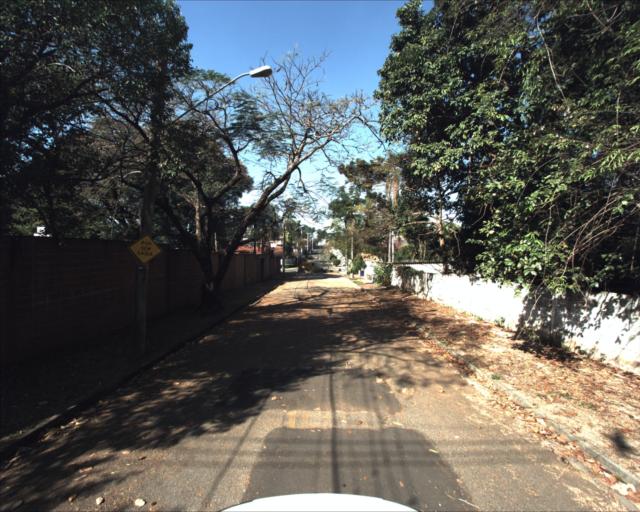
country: BR
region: Sao Paulo
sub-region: Sorocaba
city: Sorocaba
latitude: -23.4954
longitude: -47.4110
